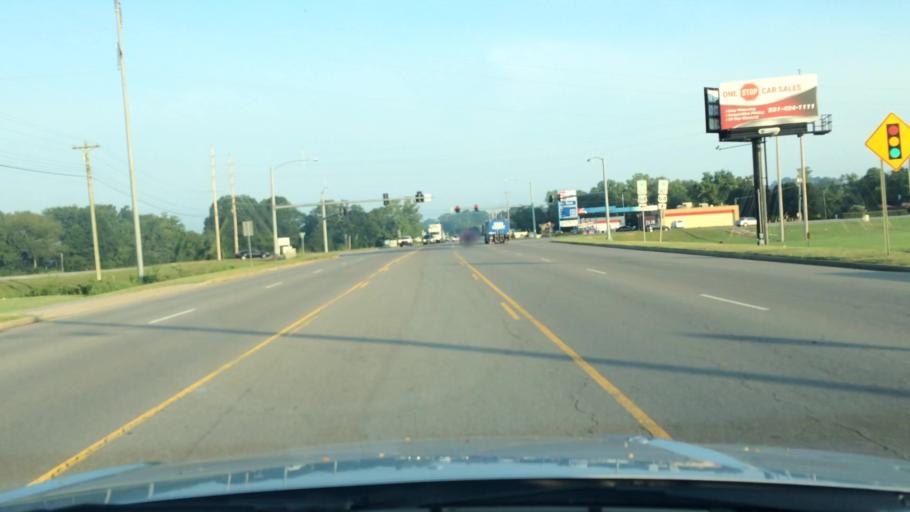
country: US
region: Tennessee
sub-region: Giles County
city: Pulaski
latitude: 35.2044
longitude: -87.0615
